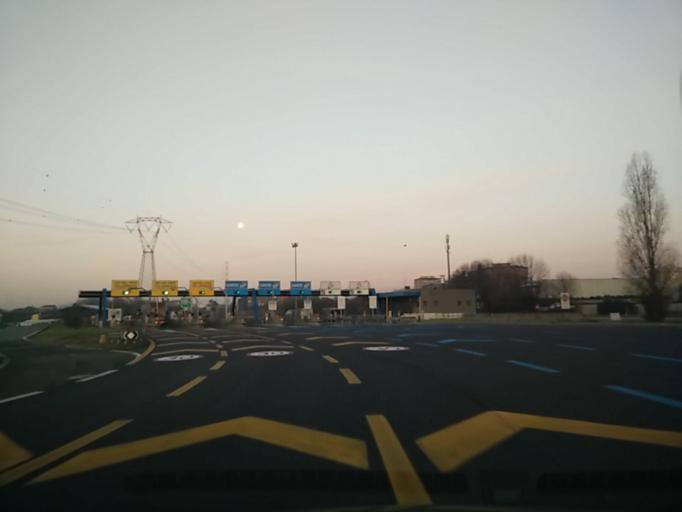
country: IT
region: Lombardy
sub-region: Provincia di Monza e Brianza
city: Monza
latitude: 45.5572
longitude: 9.2699
